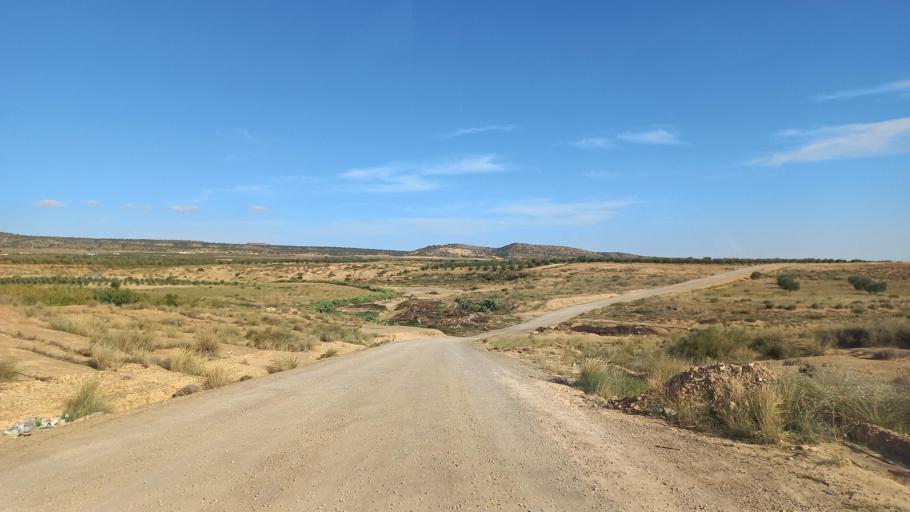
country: TN
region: Al Qasrayn
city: Sbiba
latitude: 35.3017
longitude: 9.0942
